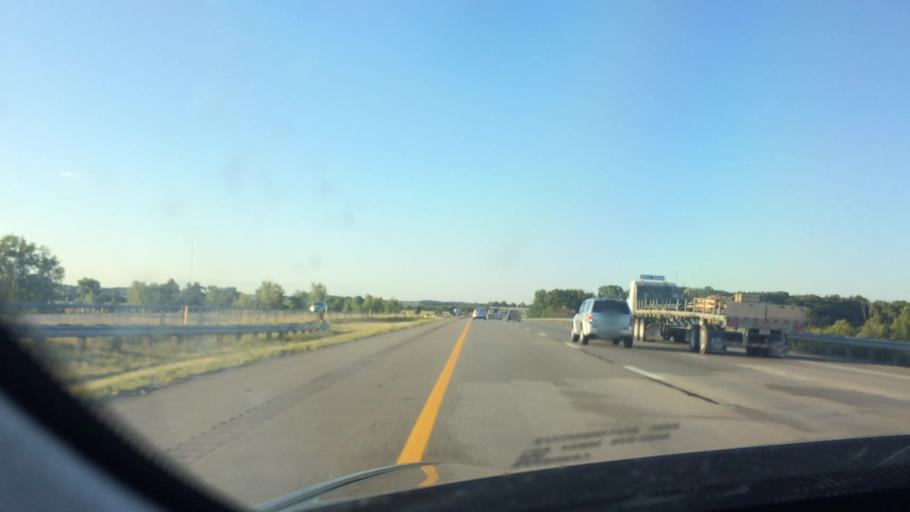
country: US
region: Ohio
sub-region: Wood County
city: Bowling Green
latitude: 41.4378
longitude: -83.6196
